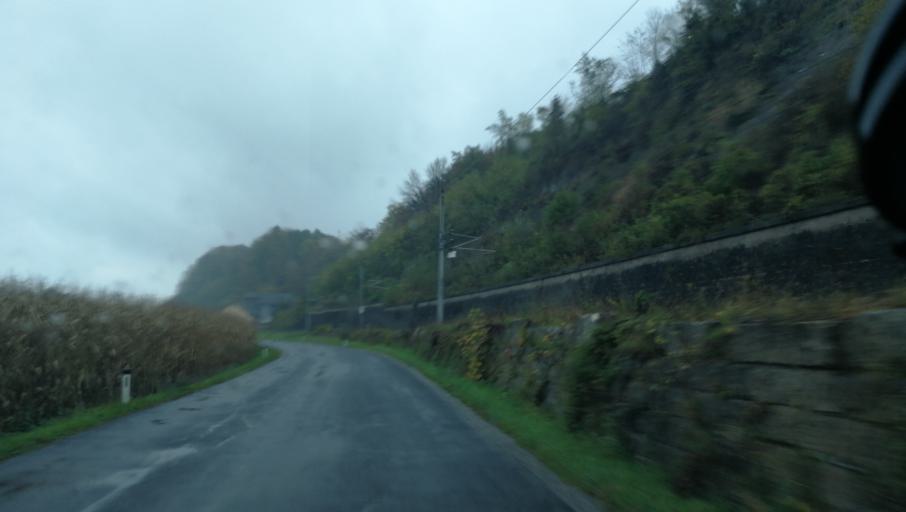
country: AT
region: Styria
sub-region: Politischer Bezirk Leibnitz
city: Ehrenhausen
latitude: 46.7232
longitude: 15.6016
